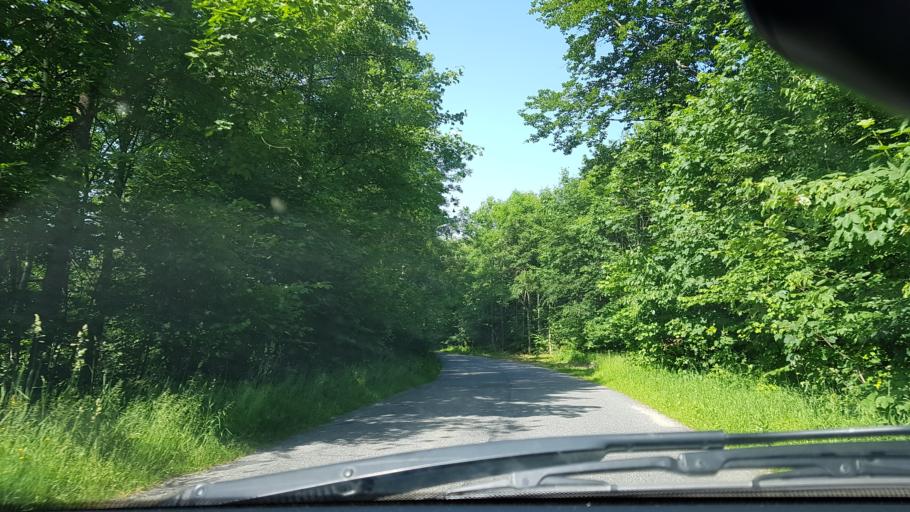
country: PL
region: Lower Silesian Voivodeship
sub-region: Powiat zabkowicki
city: Budzow
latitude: 50.5385
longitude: 16.6645
